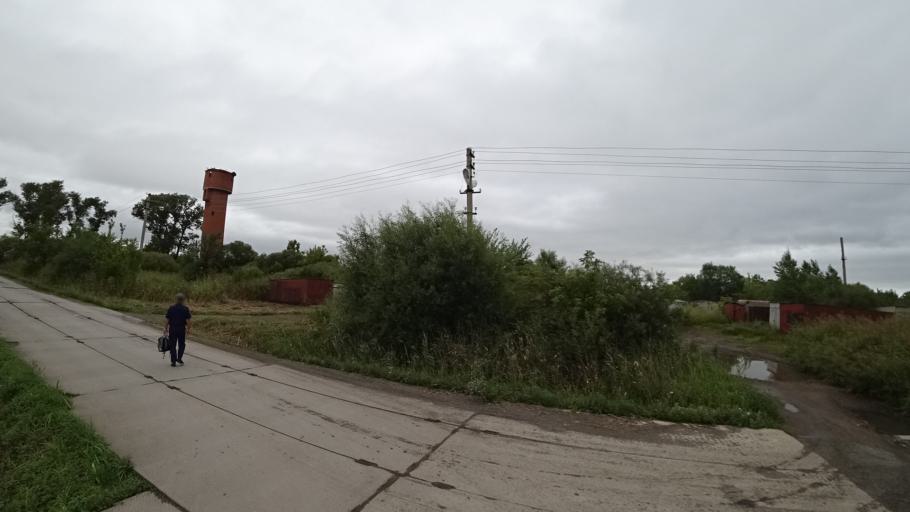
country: RU
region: Primorskiy
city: Chernigovka
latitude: 44.3341
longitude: 132.5391
